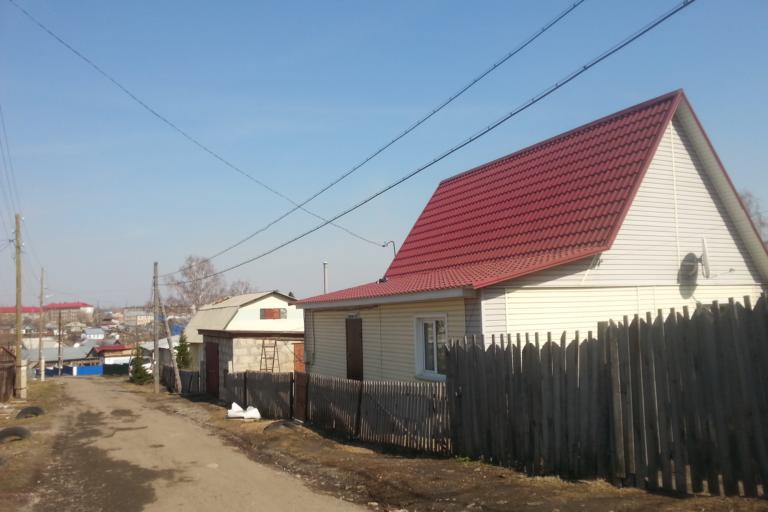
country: RU
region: Altai Krai
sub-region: Gorod Barnaulskiy
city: Barnaul
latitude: 53.3754
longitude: 83.6936
